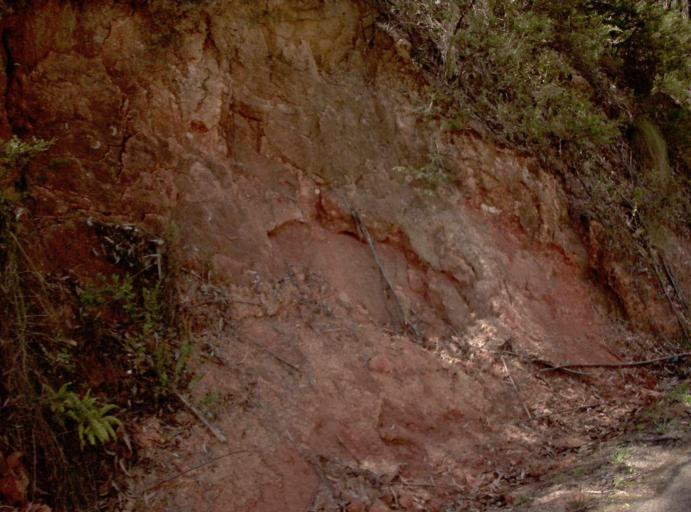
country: AU
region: New South Wales
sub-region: Bombala
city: Bombala
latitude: -37.5677
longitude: 149.3219
